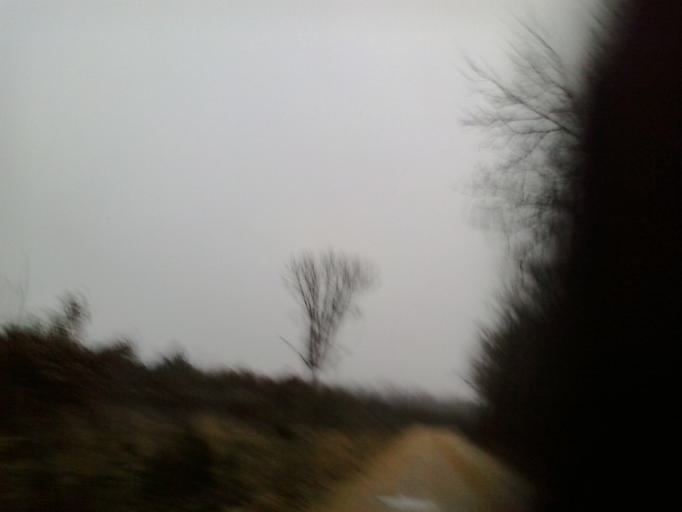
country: HU
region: Vas
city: Sarvar
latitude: 47.1403
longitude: 16.9768
